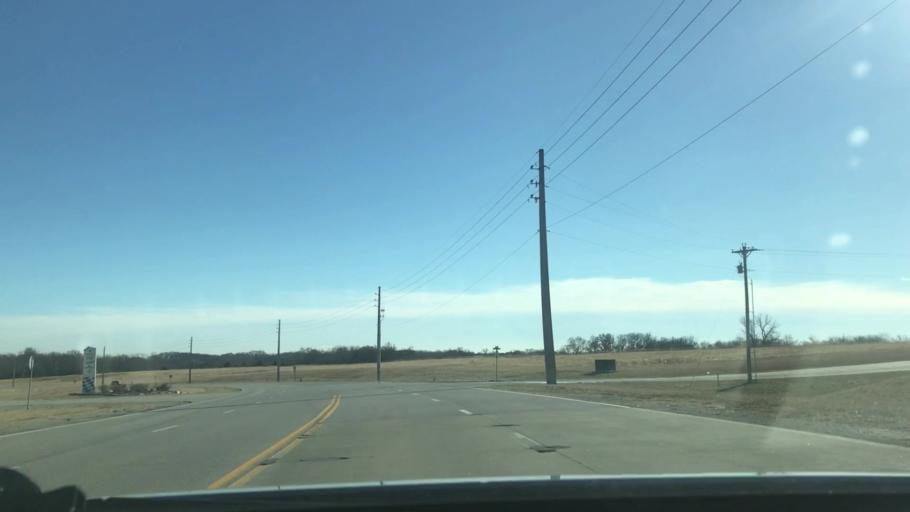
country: US
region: Kansas
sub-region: Wyandotte County
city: Bonner Springs
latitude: 39.1108
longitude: -94.8528
